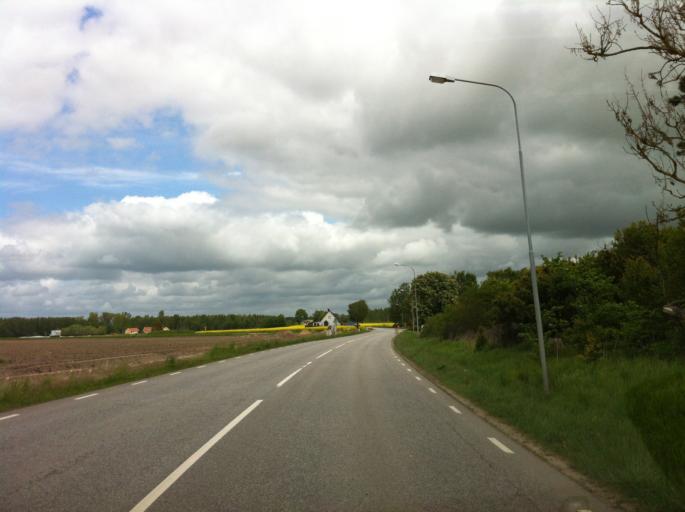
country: SE
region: Skane
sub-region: Svalovs Kommun
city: Teckomatorp
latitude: 55.8404
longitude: 13.1012
